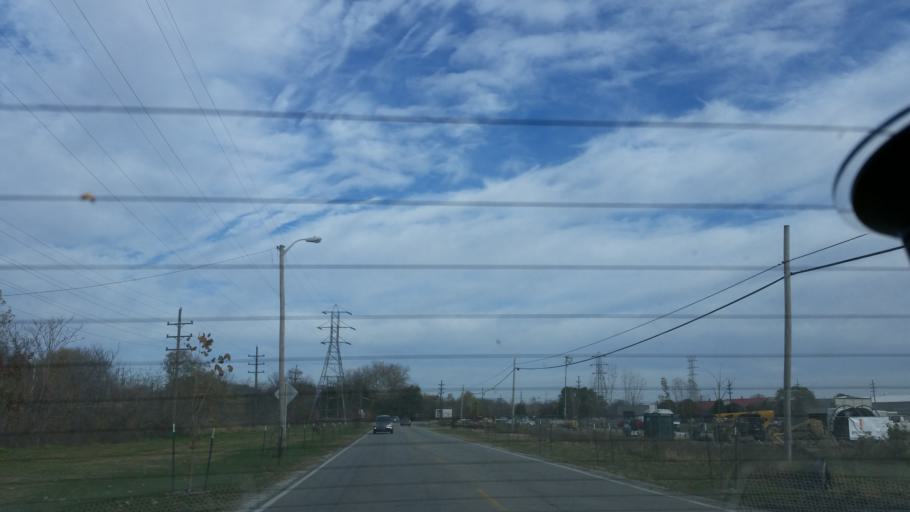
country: US
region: Indiana
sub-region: Howard County
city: Kokomo
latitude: 40.4746
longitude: -86.1490
